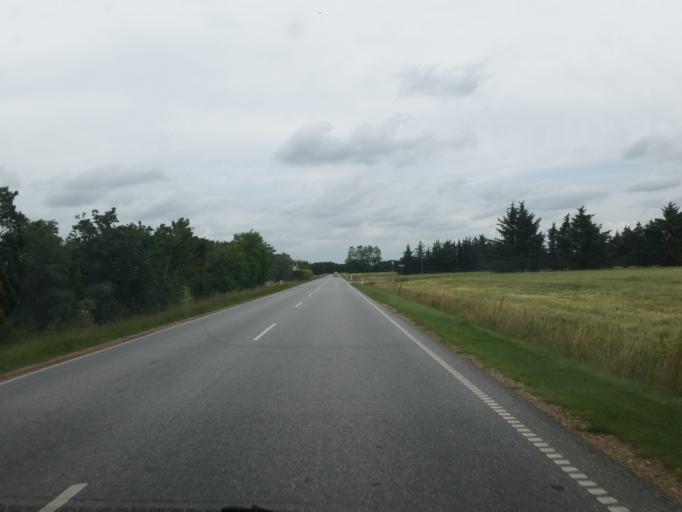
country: DK
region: South Denmark
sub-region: Esbjerg Kommune
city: Ribe
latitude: 55.3673
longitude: 8.8056
